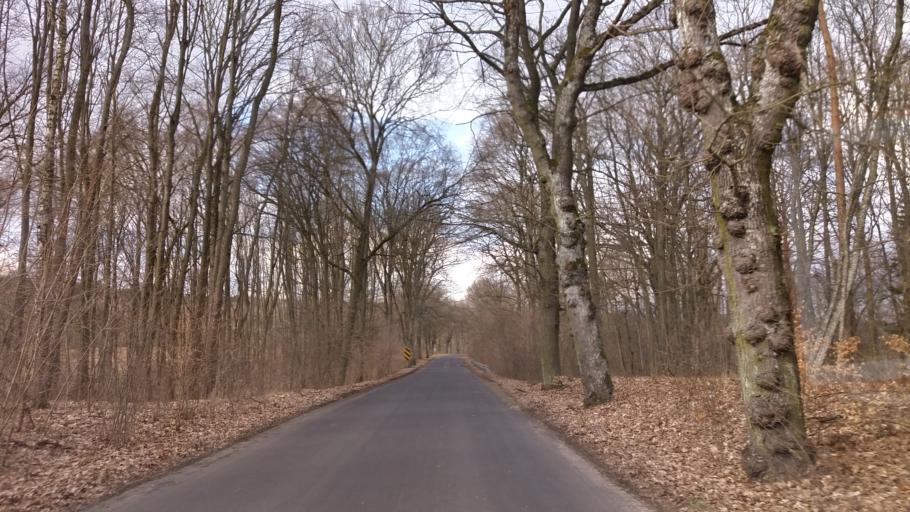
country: PL
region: West Pomeranian Voivodeship
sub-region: Powiat choszczenski
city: Recz
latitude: 53.1917
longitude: 15.6386
